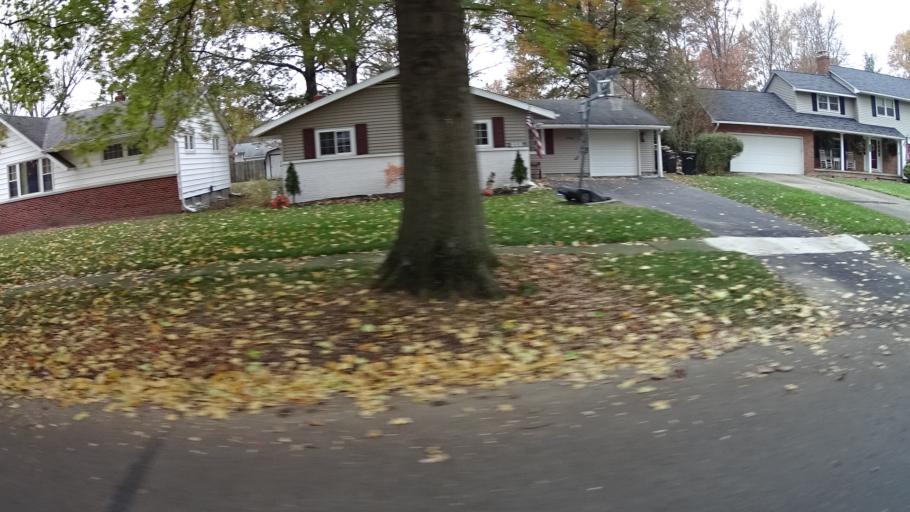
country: US
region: Ohio
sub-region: Lorain County
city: Elyria
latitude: 41.3551
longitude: -82.0984
